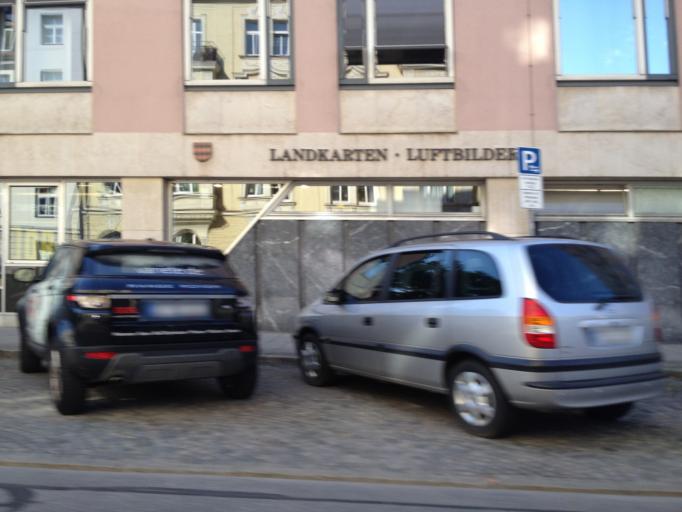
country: DE
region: Bavaria
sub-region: Upper Bavaria
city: Munich
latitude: 48.1414
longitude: 11.5914
